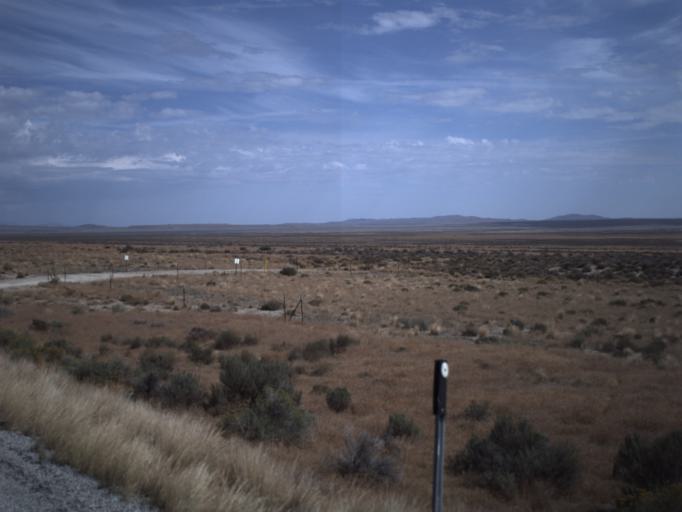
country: US
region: Utah
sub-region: Tooele County
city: Wendover
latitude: 41.5096
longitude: -113.6012
